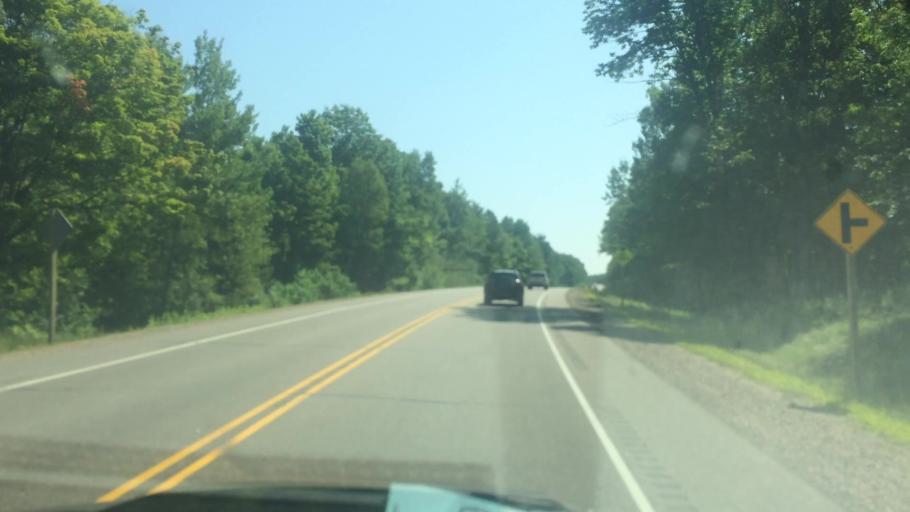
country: US
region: Wisconsin
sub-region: Oneida County
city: Rhinelander
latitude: 45.6176
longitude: -89.5211
